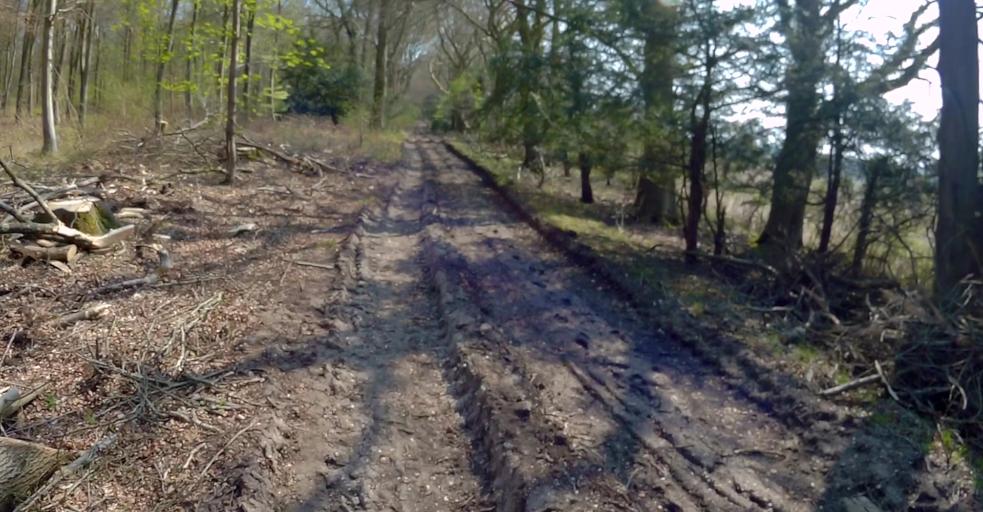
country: GB
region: England
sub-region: Hampshire
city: Overton
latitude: 51.1863
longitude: -1.2448
